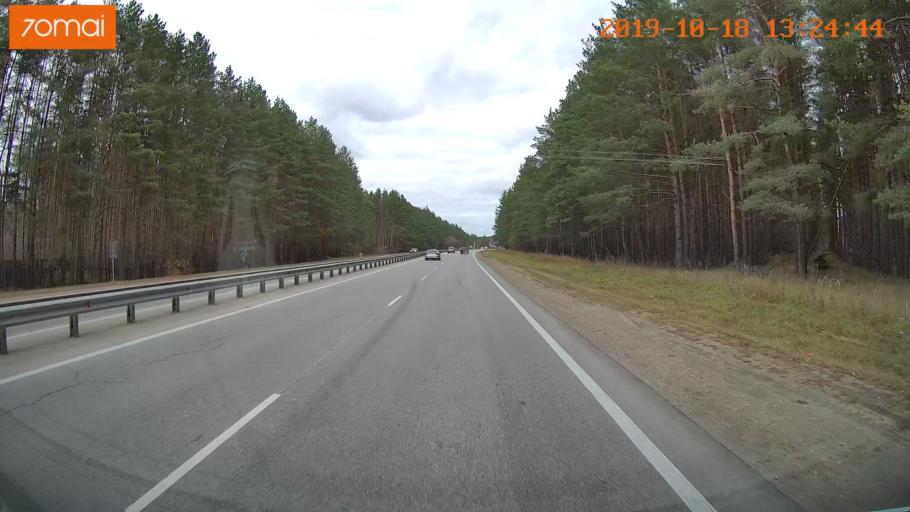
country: RU
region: Rjazan
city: Polyany
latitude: 54.7350
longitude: 39.8420
